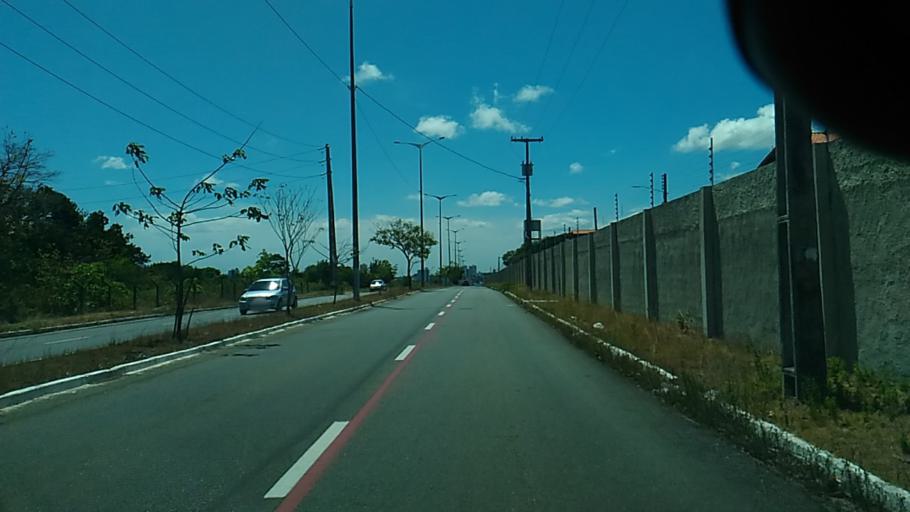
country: BR
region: Paraiba
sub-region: Joao Pessoa
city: Joao Pessoa
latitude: -7.1412
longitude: -34.8211
